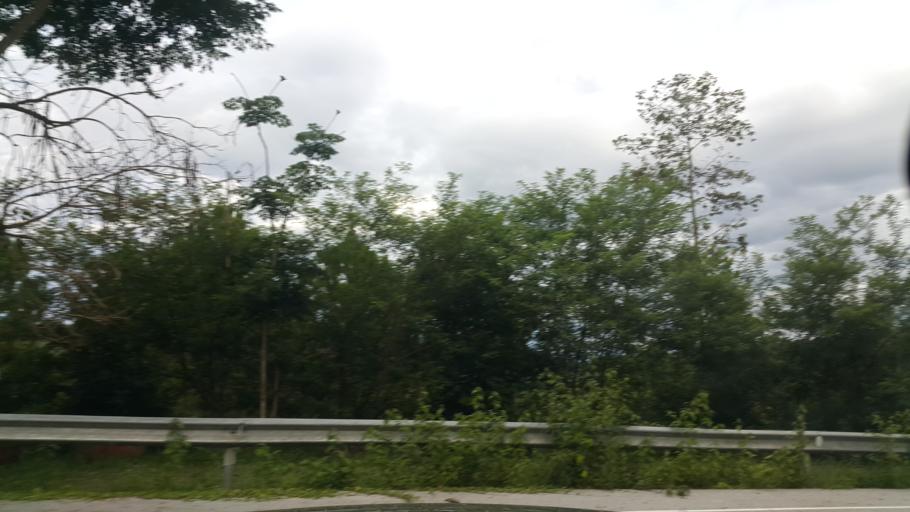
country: TH
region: Loei
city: Na Haeo
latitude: 17.5031
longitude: 101.0901
